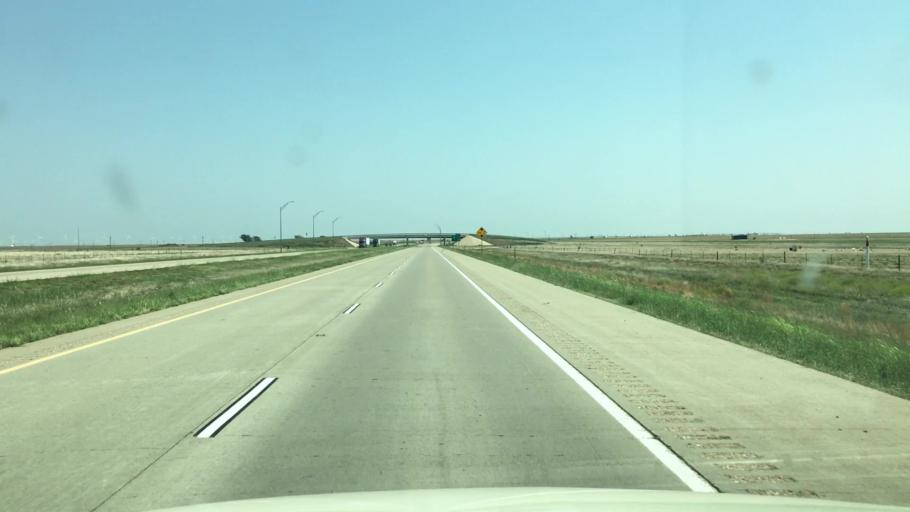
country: US
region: Texas
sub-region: Oldham County
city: Vega
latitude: 35.2376
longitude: -102.4122
